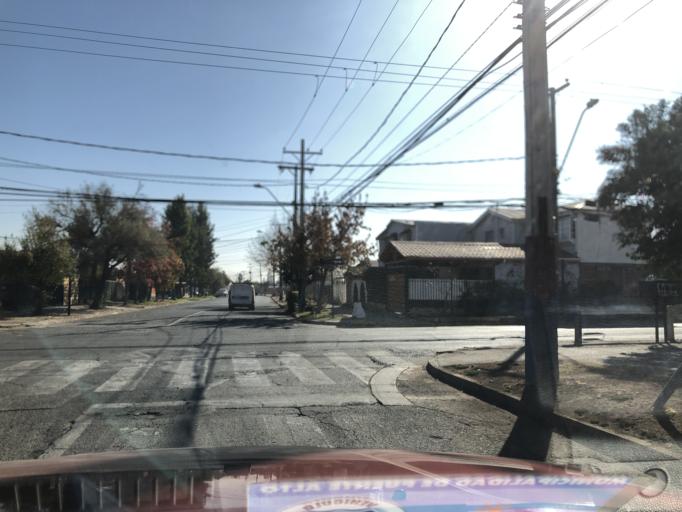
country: CL
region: Santiago Metropolitan
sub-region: Provincia de Cordillera
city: Puente Alto
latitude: -33.5919
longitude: -70.5735
